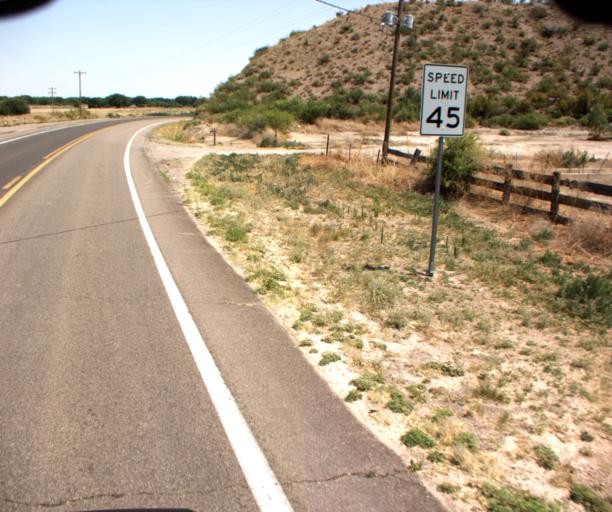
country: US
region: Arizona
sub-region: Greenlee County
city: Clifton
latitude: 32.7310
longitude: -109.1134
